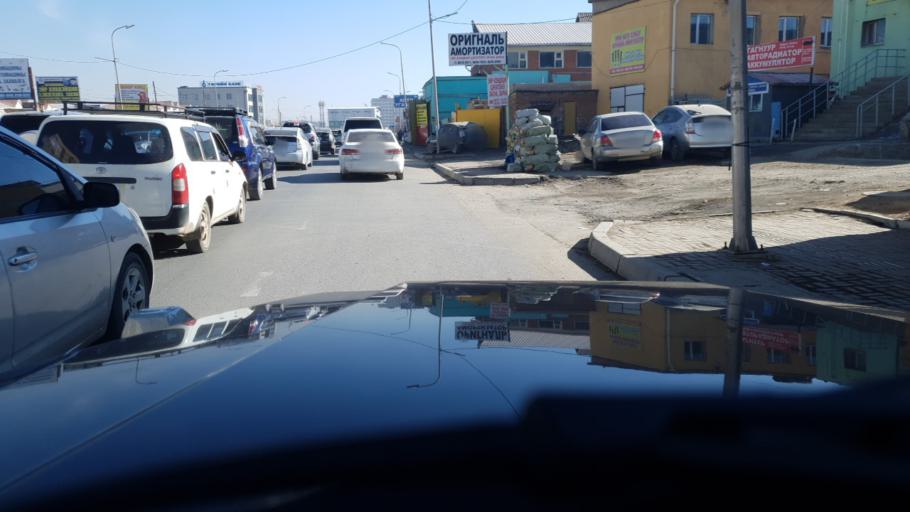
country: MN
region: Ulaanbaatar
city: Ulaanbaatar
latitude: 47.9241
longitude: 106.9687
